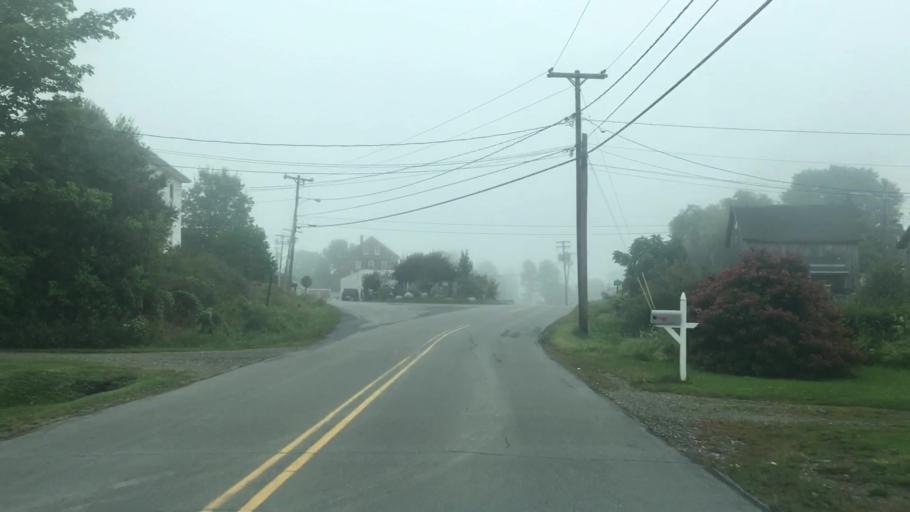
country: US
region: Maine
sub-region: Waldo County
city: Stockton Springs
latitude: 44.4599
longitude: -68.9275
